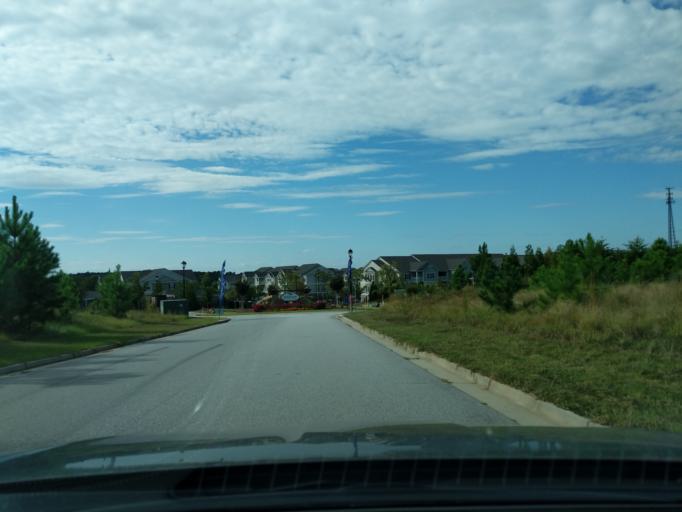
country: US
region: Georgia
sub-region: Columbia County
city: Grovetown
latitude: 33.4804
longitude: -82.2026
